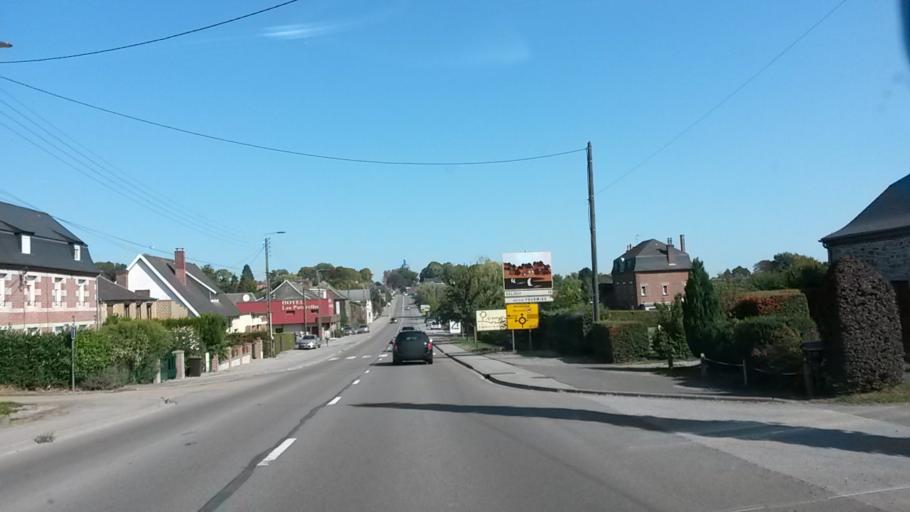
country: FR
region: Nord-Pas-de-Calais
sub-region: Departement du Nord
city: Avesnes-sur-Helpe
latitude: 50.1135
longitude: 3.9319
